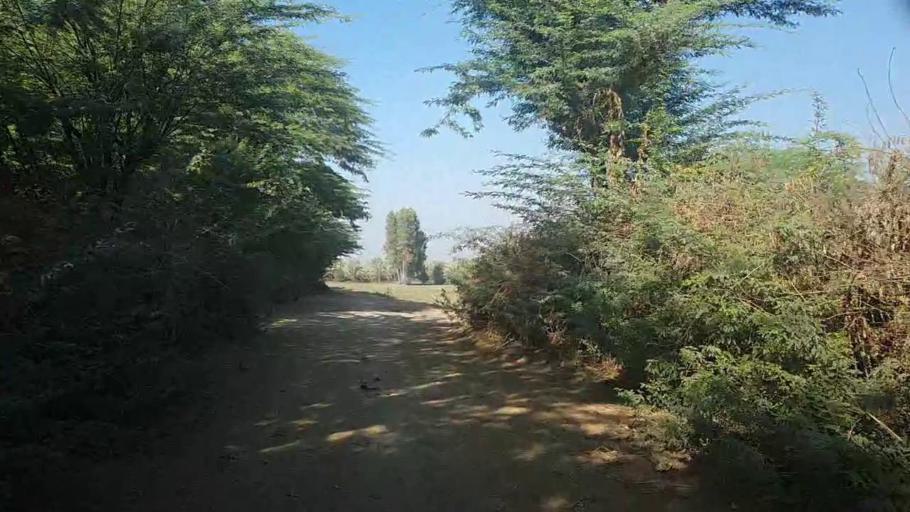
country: PK
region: Sindh
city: Kot Diji
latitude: 27.4303
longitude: 68.7377
